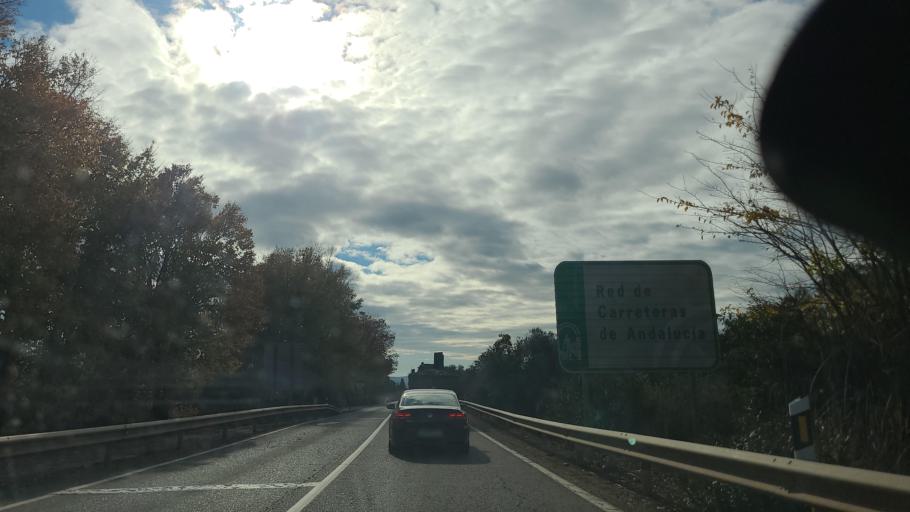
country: ES
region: Andalusia
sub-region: Provincia de Jaen
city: Villanueva de la Reina
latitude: 38.0460
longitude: -3.9100
